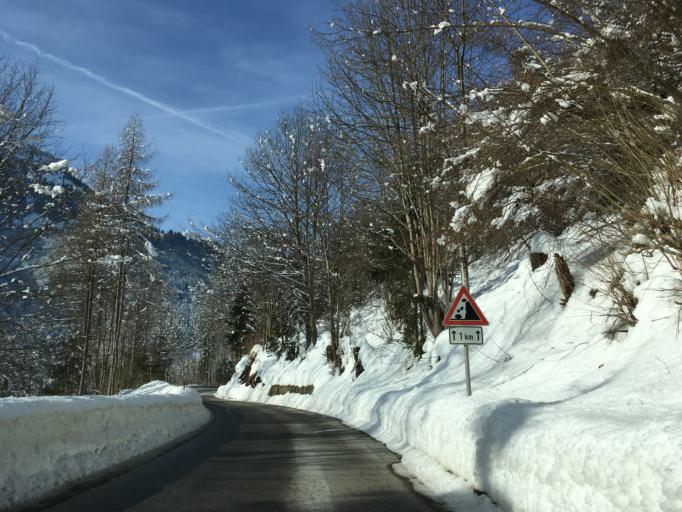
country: DE
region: Bavaria
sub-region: Upper Bavaria
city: Burg Unter-Falkenstein
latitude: 47.6581
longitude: 12.1230
